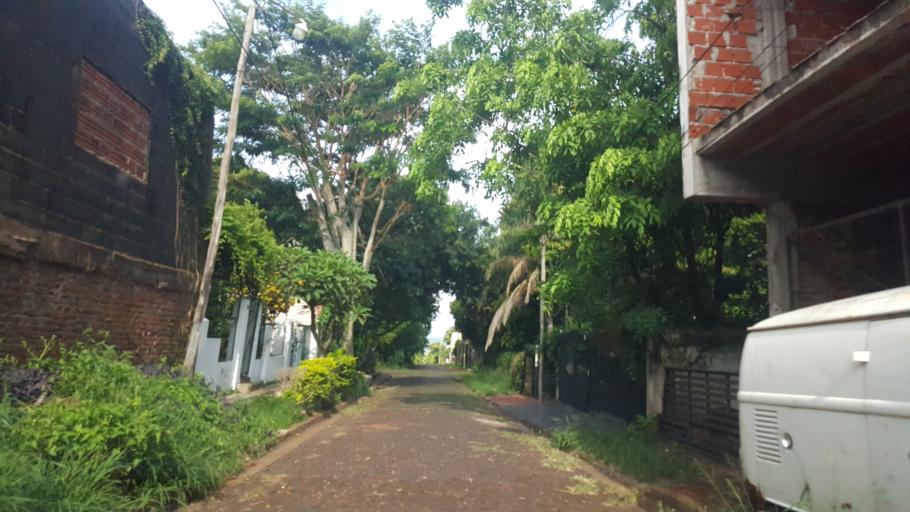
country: AR
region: Misiones
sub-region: Departamento de Capital
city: Posadas
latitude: -27.3876
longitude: -55.8925
